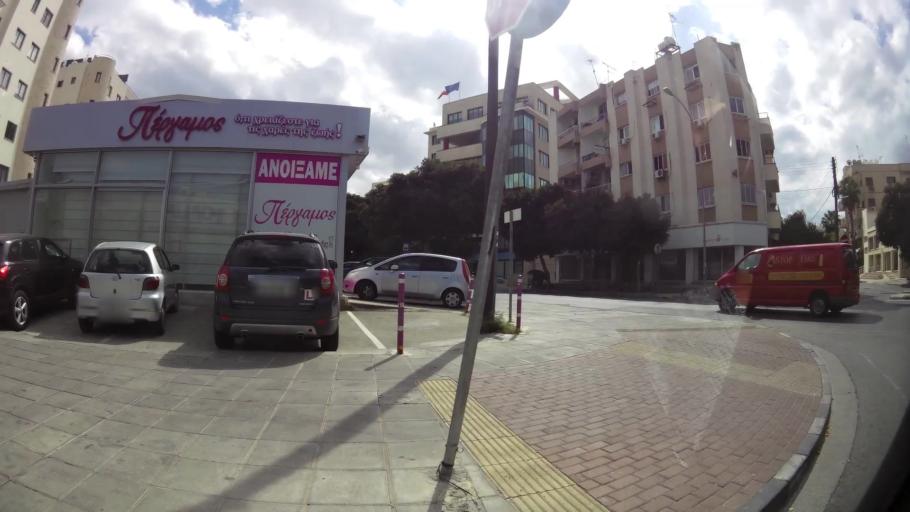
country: CY
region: Lefkosia
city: Nicosia
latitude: 35.1608
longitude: 33.3596
